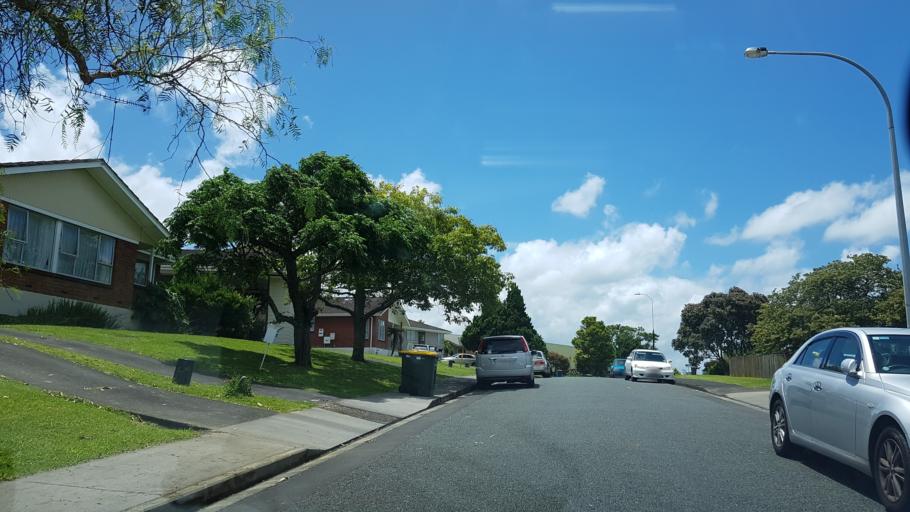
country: NZ
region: Auckland
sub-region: Auckland
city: North Shore
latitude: -36.7985
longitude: 174.7433
